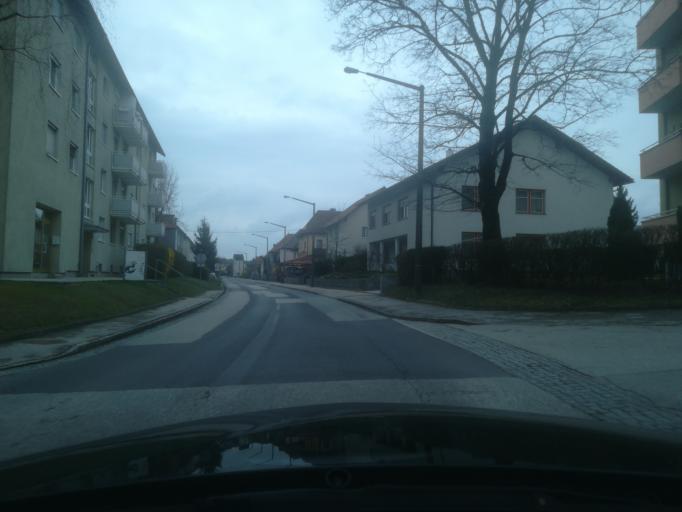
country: AT
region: Upper Austria
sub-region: Politischer Bezirk Urfahr-Umgebung
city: Feldkirchen an der Donau
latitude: 48.3044
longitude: 14.0220
